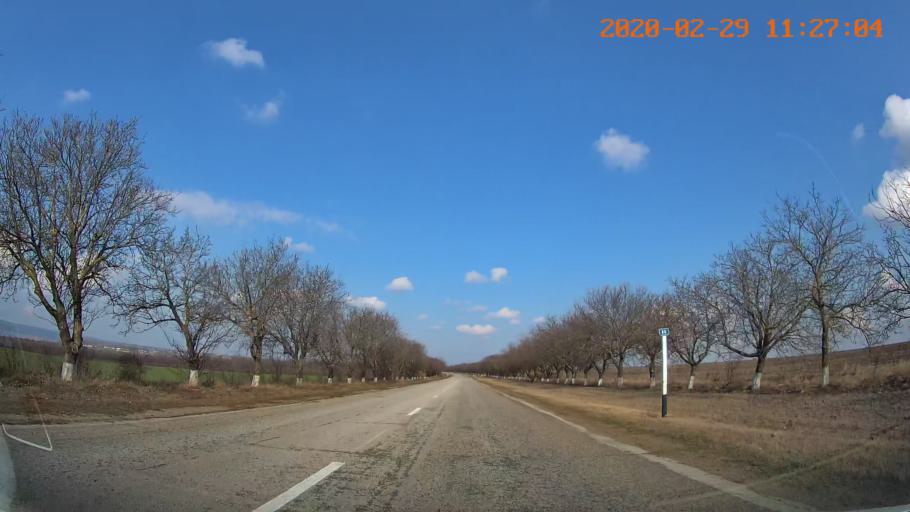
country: MD
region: Telenesti
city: Cocieri
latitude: 47.4625
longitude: 29.1438
